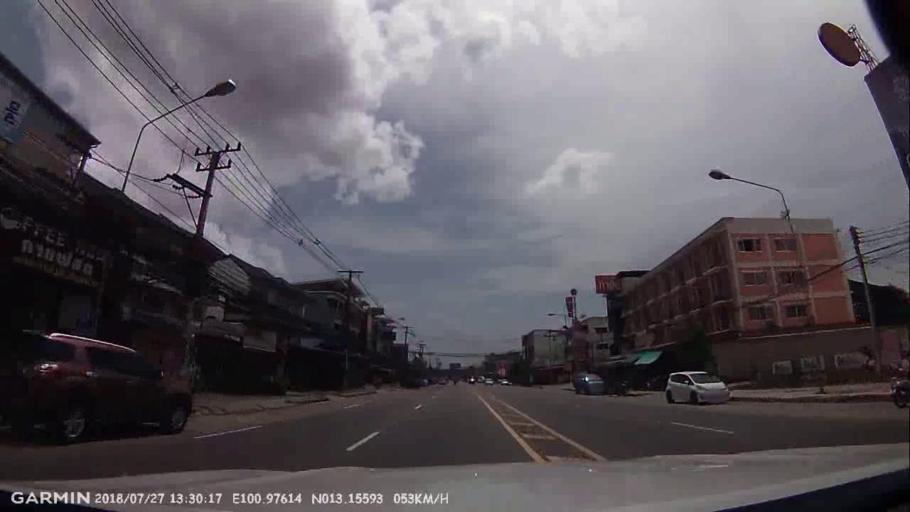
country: TH
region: Chon Buri
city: Si Racha
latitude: 13.1560
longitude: 100.9760
